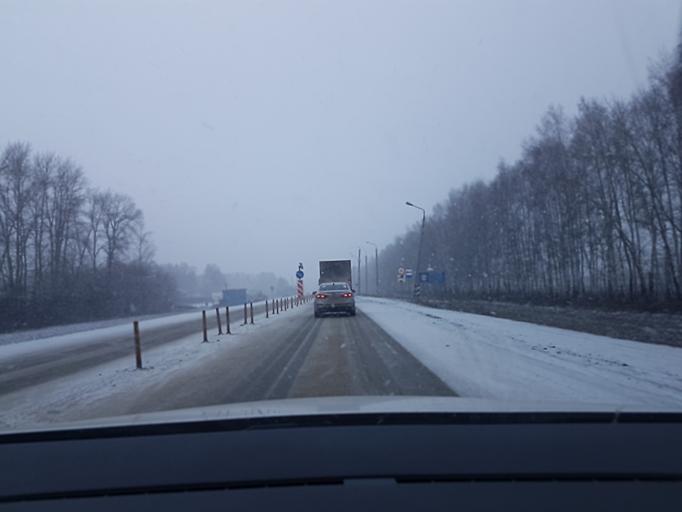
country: RU
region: Tambov
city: Pervomayskiy
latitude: 53.3099
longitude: 40.2203
